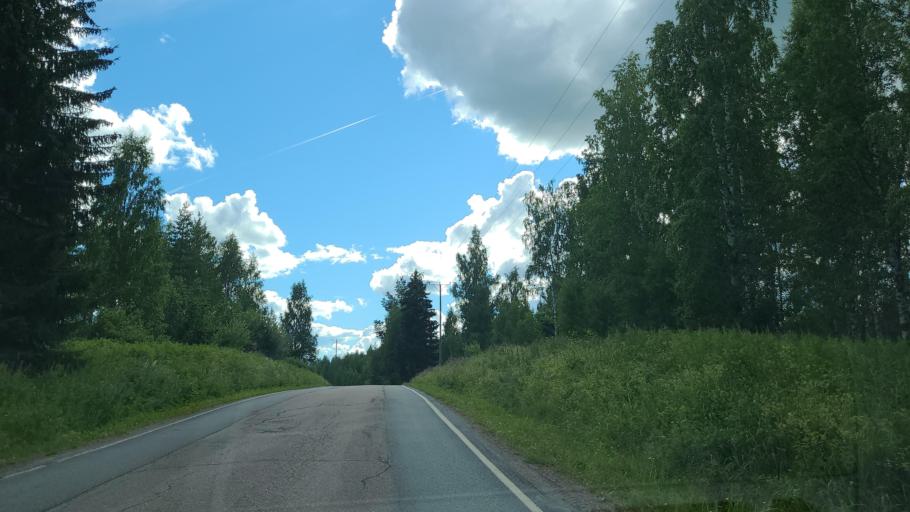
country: FI
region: Central Finland
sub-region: Jaemsae
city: Jaemsae
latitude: 61.8977
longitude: 25.2669
